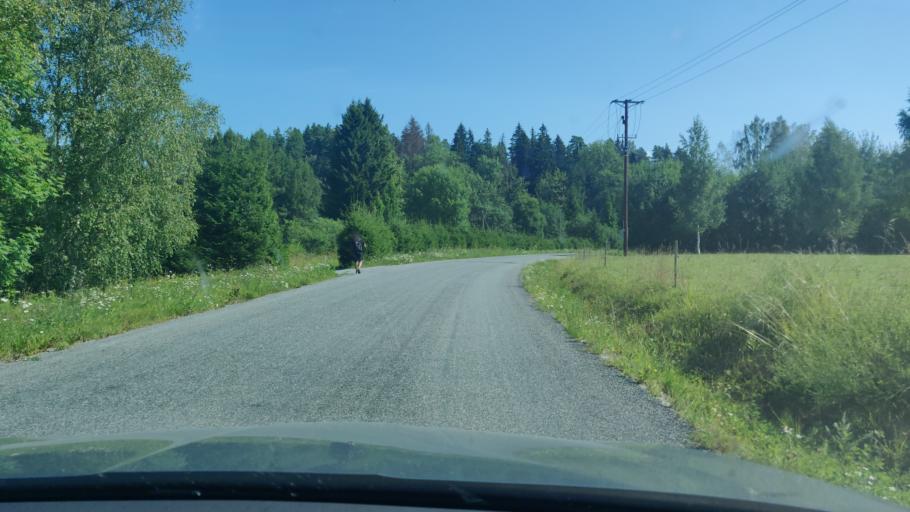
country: EE
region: Tartu
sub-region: Elva linn
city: Elva
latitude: 58.1202
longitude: 26.4671
